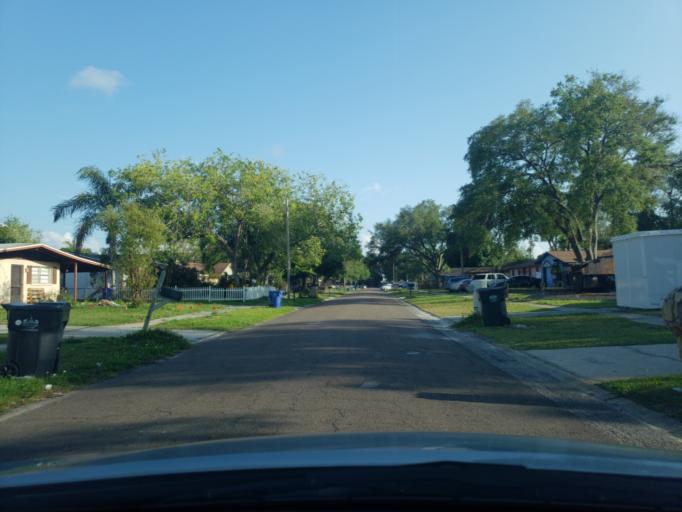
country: US
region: Florida
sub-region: Hillsborough County
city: Palm River-Clair Mel
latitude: 27.9180
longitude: -82.3648
